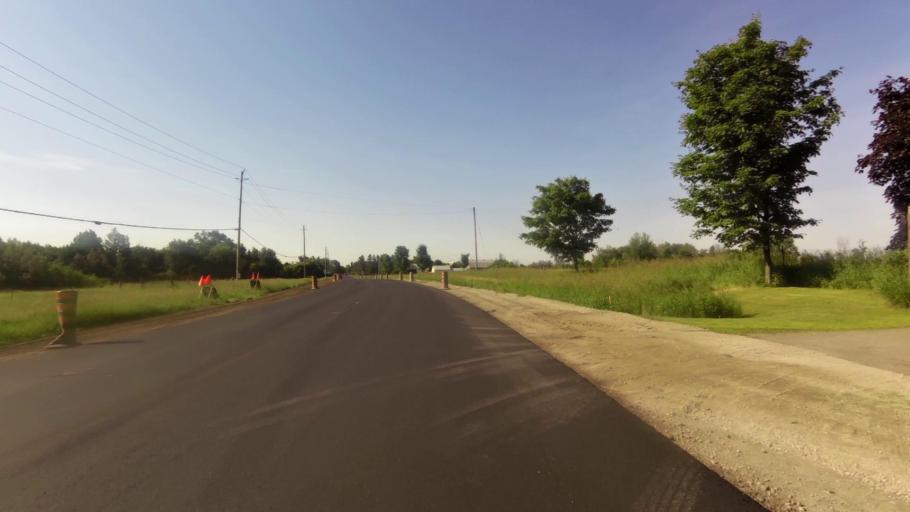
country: CA
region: Ontario
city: Ottawa
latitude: 45.2055
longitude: -75.5695
